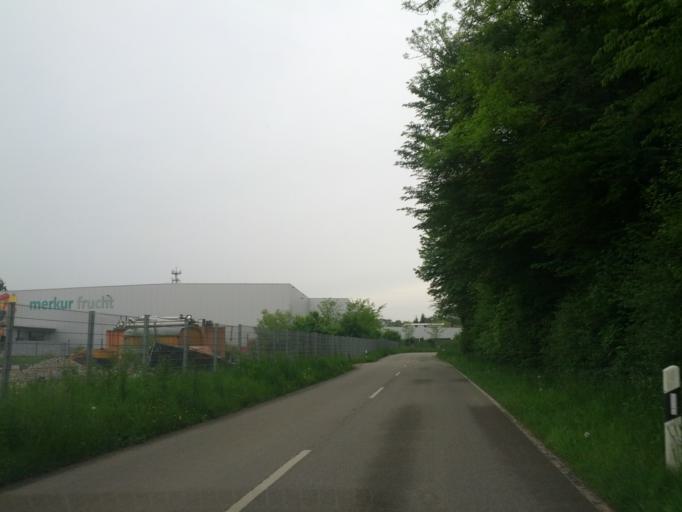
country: DE
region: Baden-Wuerttemberg
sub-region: Freiburg Region
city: Umkirch
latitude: 48.0405
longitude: 7.7580
